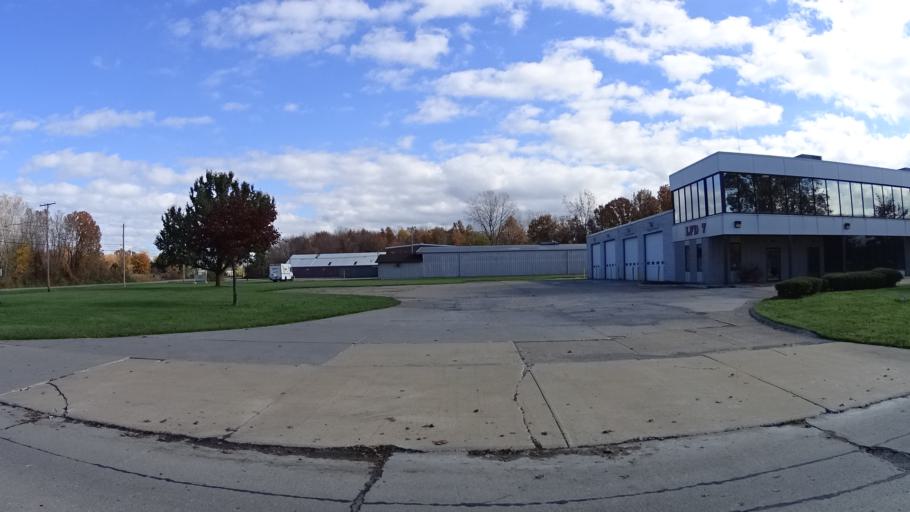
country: US
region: Ohio
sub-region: Lorain County
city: Lorain
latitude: 41.4495
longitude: -82.2125
